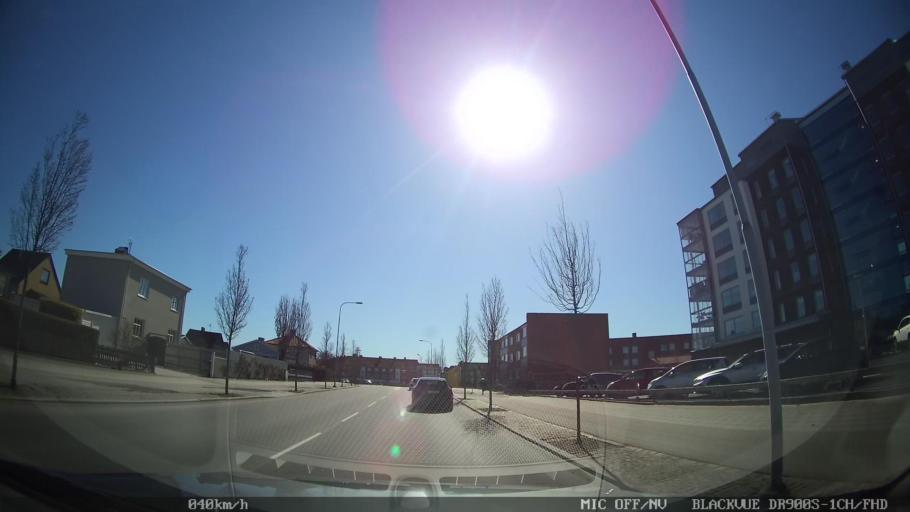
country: SE
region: Skane
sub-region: Ystads Kommun
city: Ystad
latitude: 55.4301
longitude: 13.8048
